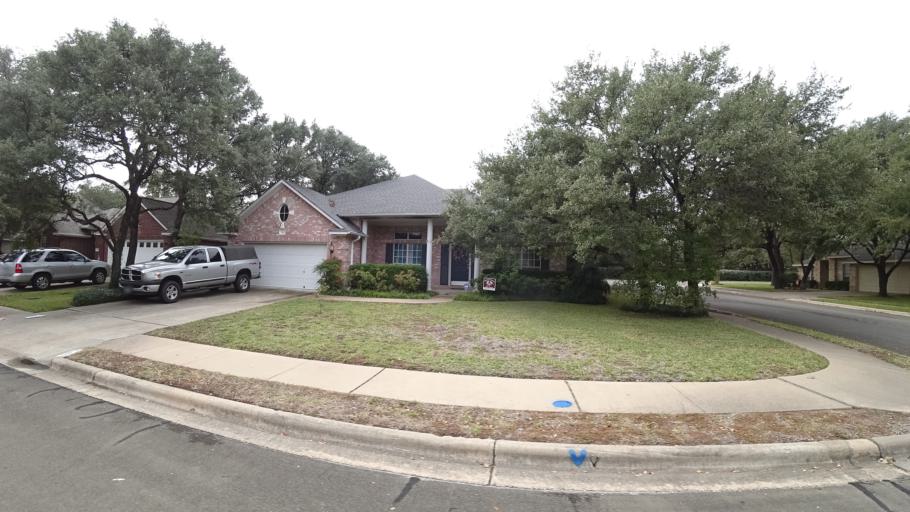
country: US
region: Texas
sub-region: Williamson County
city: Brushy Creek
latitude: 30.5154
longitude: -97.7102
